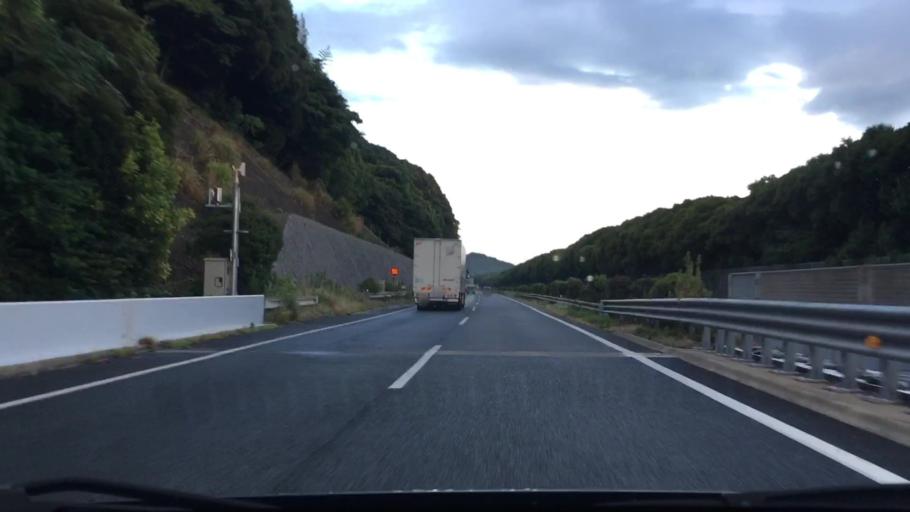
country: JP
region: Yamaguchi
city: Shimonoseki
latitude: 33.8675
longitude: 130.9561
